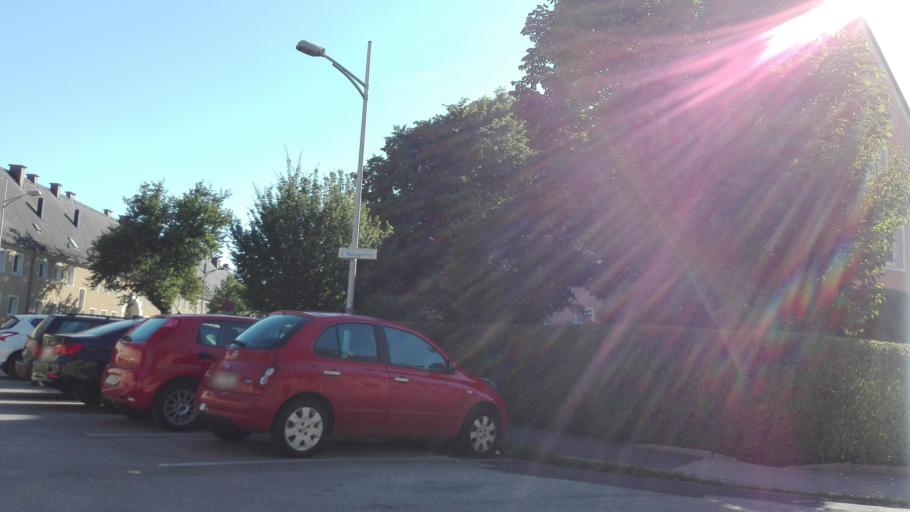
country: AT
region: Upper Austria
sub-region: Linz Stadt
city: Linz
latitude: 48.2728
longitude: 14.3008
